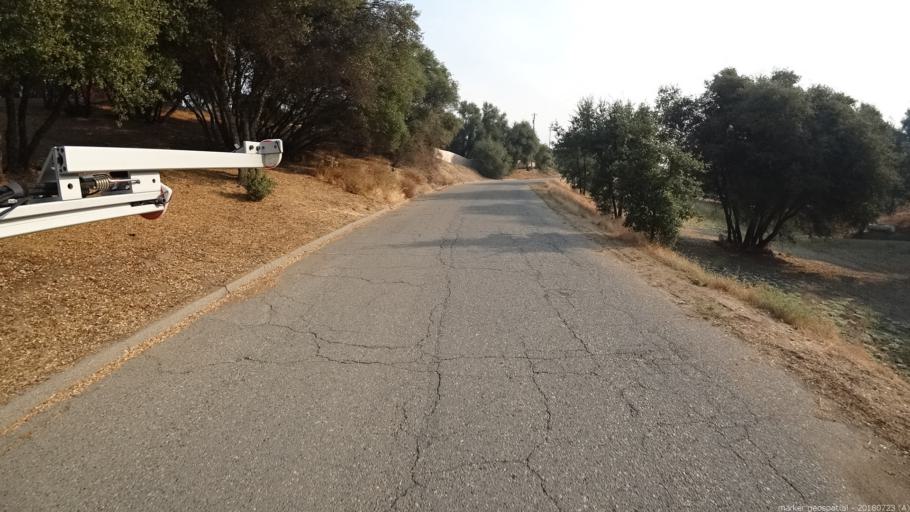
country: US
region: California
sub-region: Madera County
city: Ahwahnee
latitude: 37.3701
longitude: -119.7329
